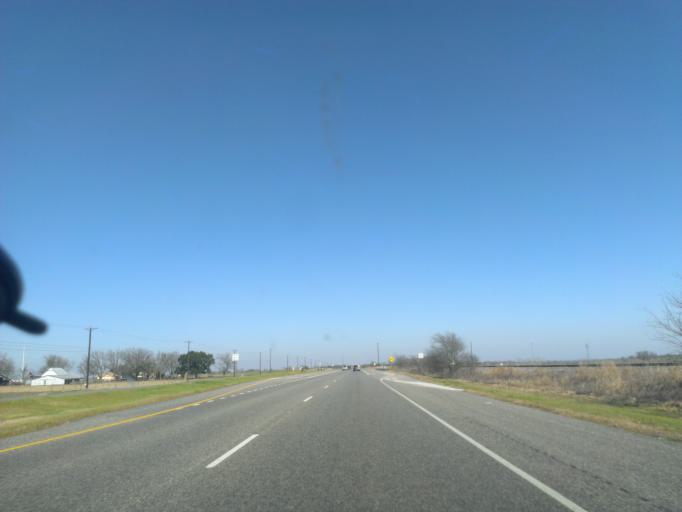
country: US
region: Texas
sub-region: Williamson County
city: Taylor
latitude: 30.5830
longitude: -97.3389
